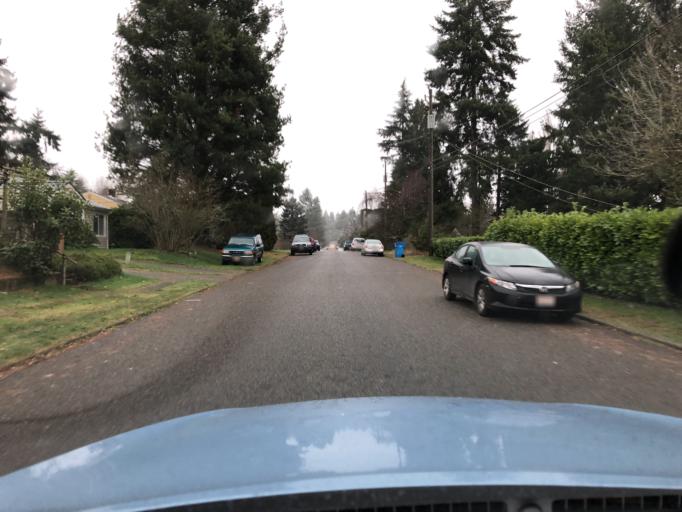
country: US
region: Washington
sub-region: King County
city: Lake Forest Park
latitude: 47.7431
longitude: -122.2994
